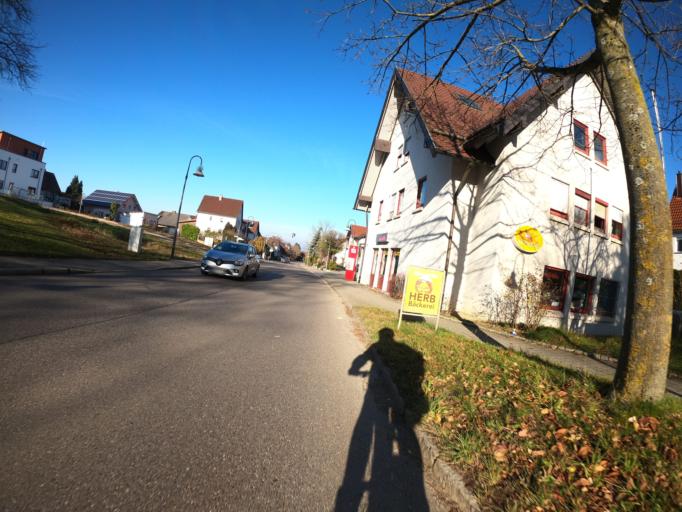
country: DE
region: Baden-Wuerttemberg
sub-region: Regierungsbezirk Stuttgart
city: Gammelshausen
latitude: 48.6407
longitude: 9.6507
